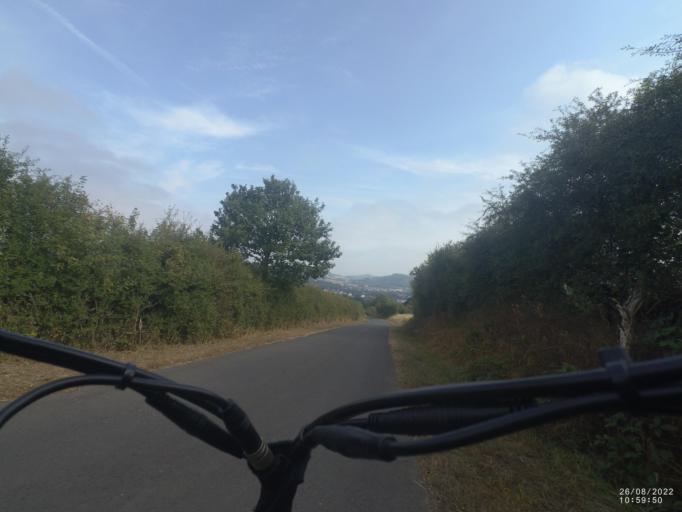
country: DE
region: Rheinland-Pfalz
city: Birresborn
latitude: 50.2081
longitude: 6.6260
